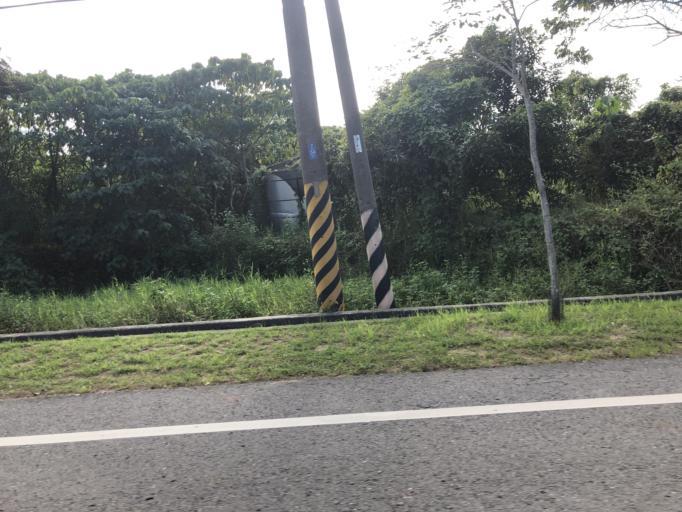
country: TW
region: Taiwan
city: Yujing
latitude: 23.0478
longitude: 120.4236
